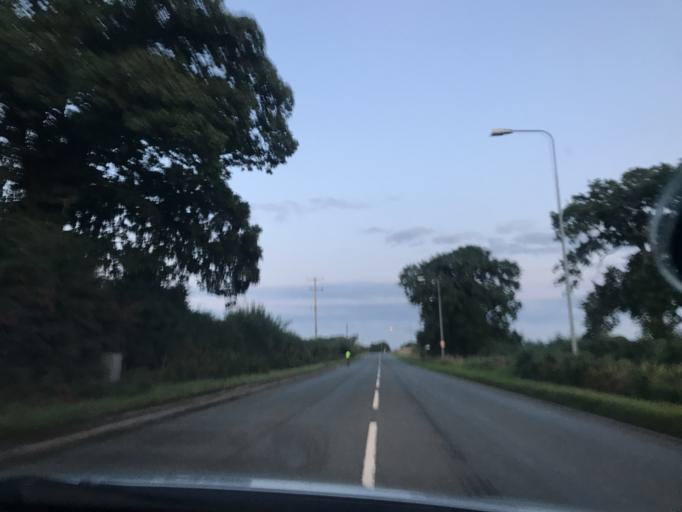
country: GB
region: England
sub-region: Cheshire West and Chester
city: Kelsall
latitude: 53.2117
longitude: -2.6799
